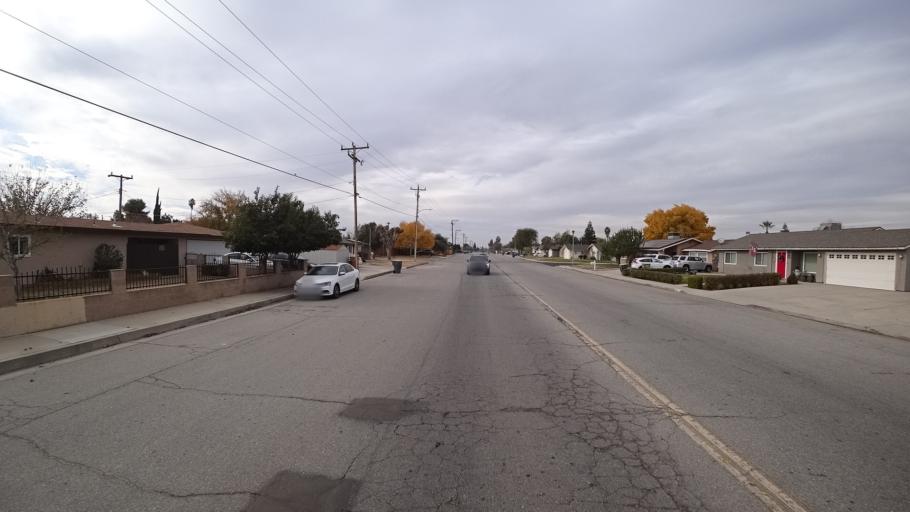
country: US
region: California
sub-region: Kern County
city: Greenacres
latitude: 35.3907
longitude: -119.1220
